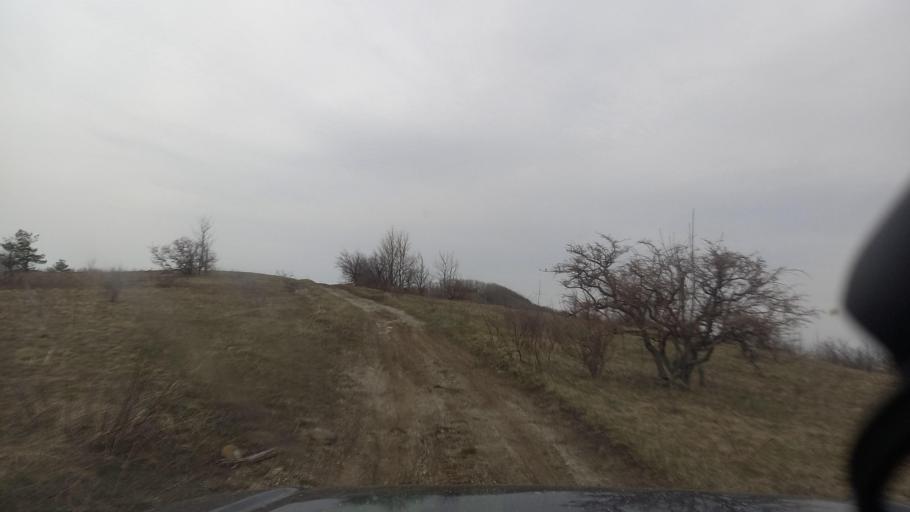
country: RU
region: Krasnodarskiy
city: Pshada
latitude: 44.5979
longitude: 38.2855
